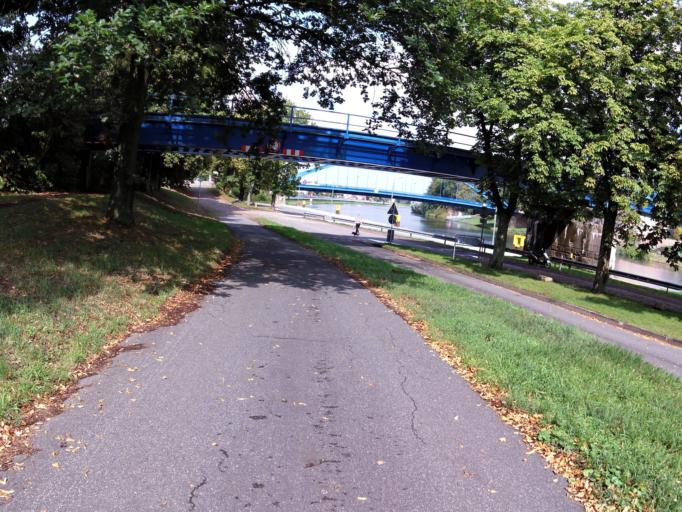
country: DE
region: Lower Saxony
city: Hoya
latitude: 52.8040
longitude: 9.1451
